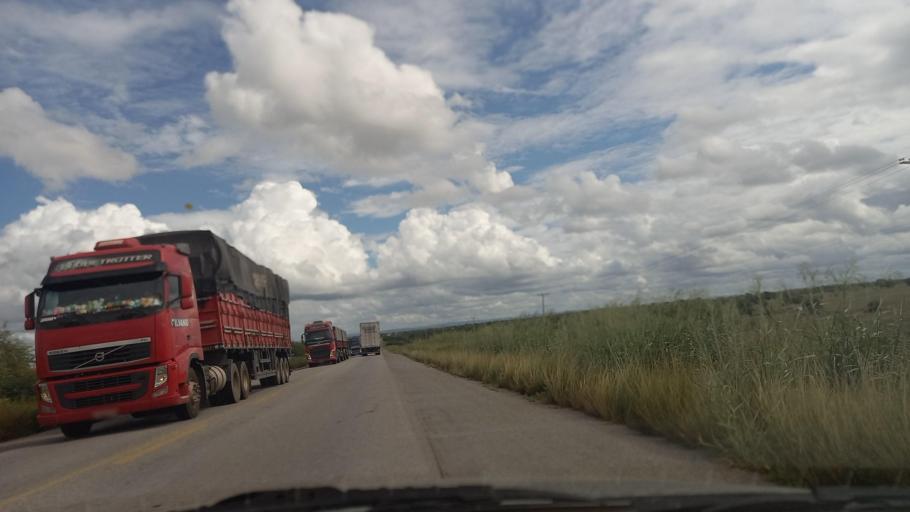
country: BR
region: Pernambuco
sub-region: Cachoeirinha
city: Cachoeirinha
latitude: -8.4207
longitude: -36.1946
